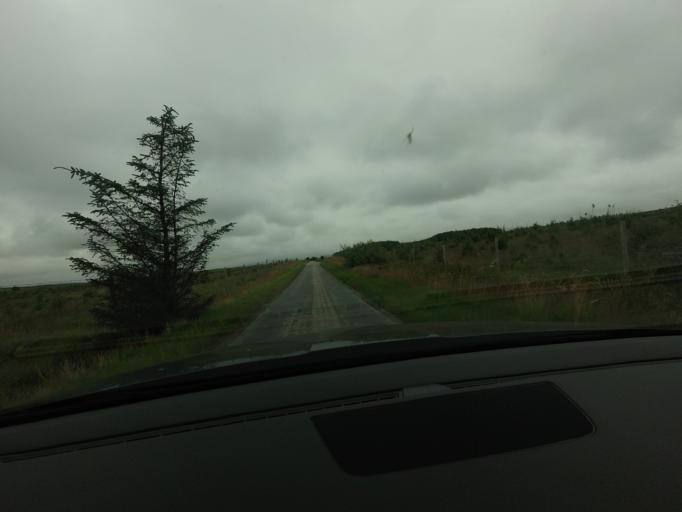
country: GB
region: Scotland
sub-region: Highland
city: Alness
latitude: 58.0675
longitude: -4.4151
